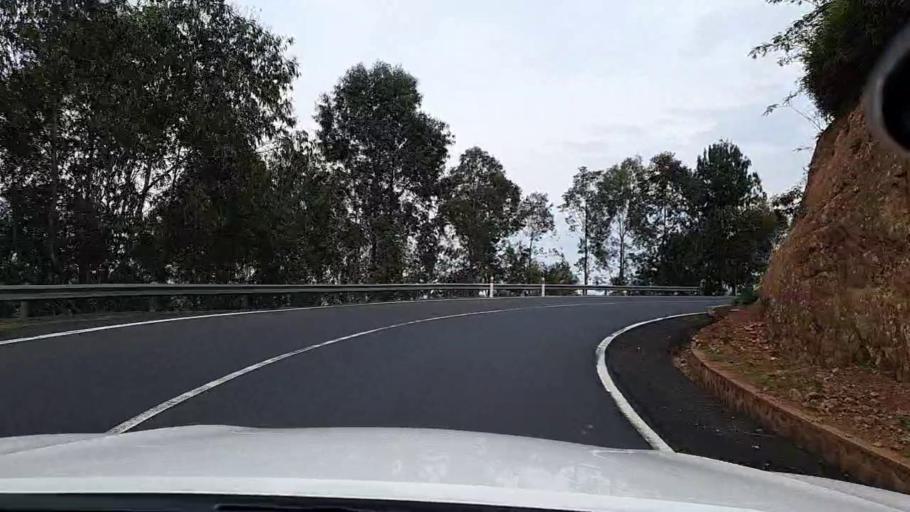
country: RW
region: Western Province
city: Kibuye
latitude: -2.1795
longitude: 29.2893
